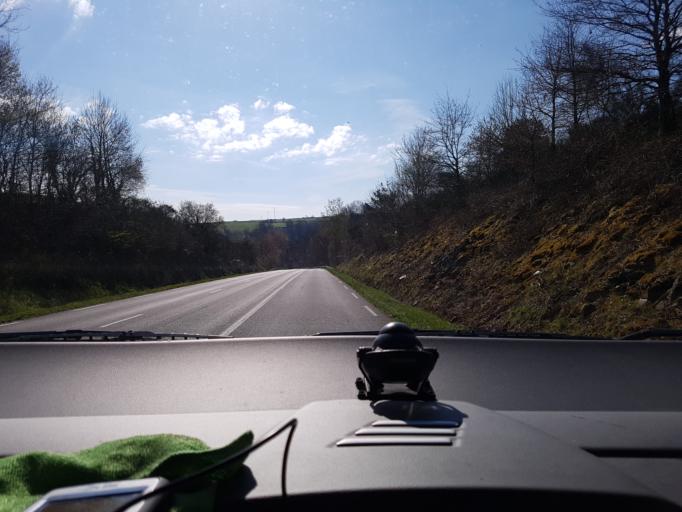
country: FR
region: Midi-Pyrenees
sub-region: Departement de l'Aveyron
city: Moyrazes
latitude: 44.3807
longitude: 2.4109
